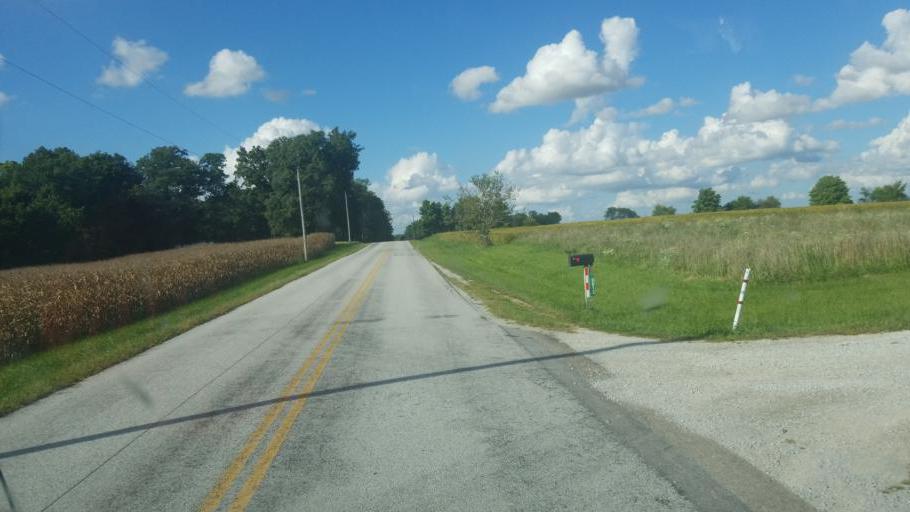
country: US
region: Ohio
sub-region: Hardin County
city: Ada
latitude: 40.7237
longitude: -83.7299
